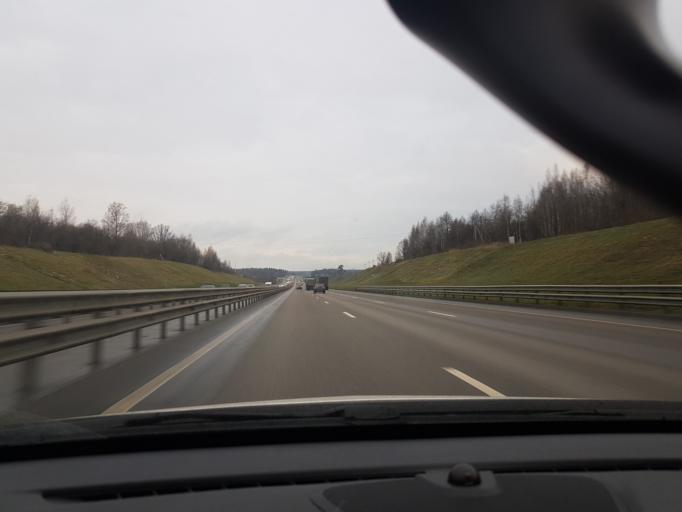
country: RU
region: Moskovskaya
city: Rumyantsevo
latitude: 55.9216
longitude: 36.5843
